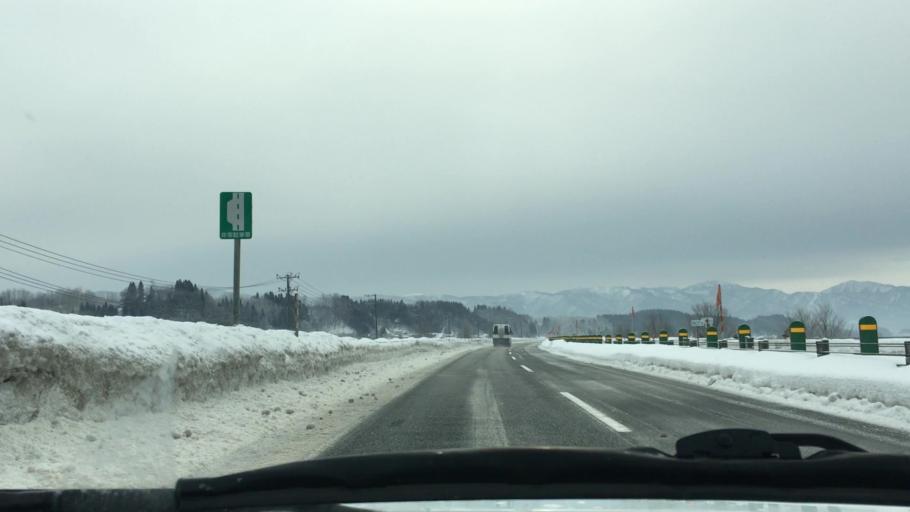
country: JP
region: Akita
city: Hanawa
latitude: 40.2976
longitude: 140.7520
